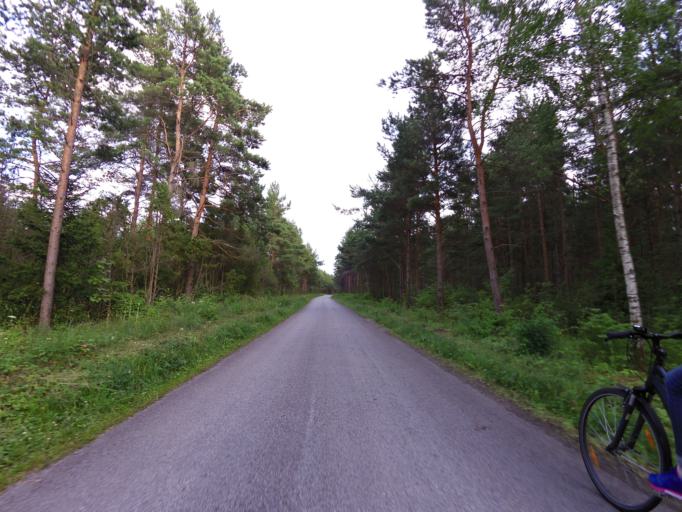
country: EE
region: Laeaene
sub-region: Vormsi vald
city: Hullo
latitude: 58.9806
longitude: 23.2512
